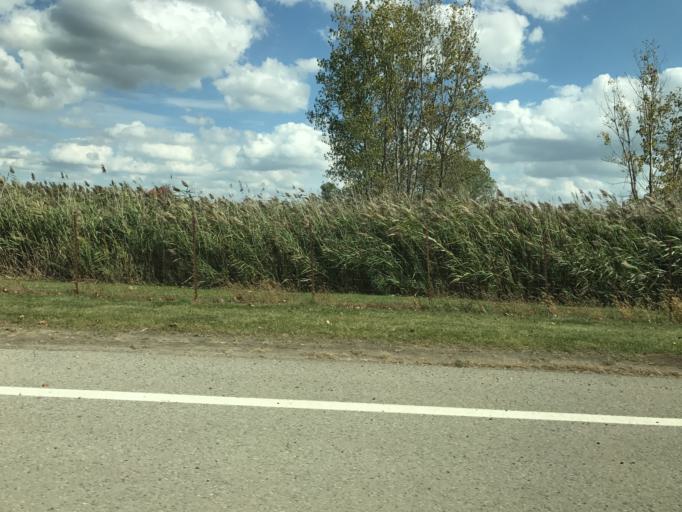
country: US
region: Michigan
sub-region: Oakland County
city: South Lyon
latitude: 42.4929
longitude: -83.6144
